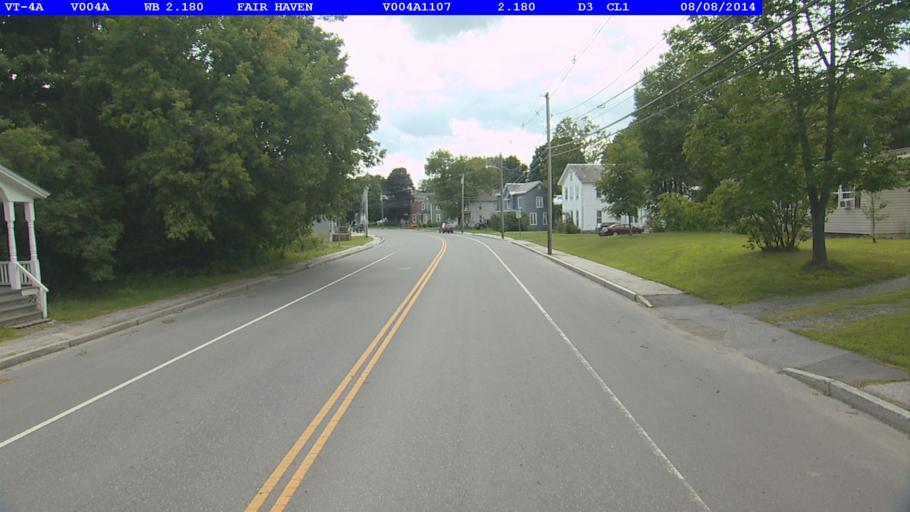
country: US
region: Vermont
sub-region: Rutland County
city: Fair Haven
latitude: 43.5992
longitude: -73.2628
